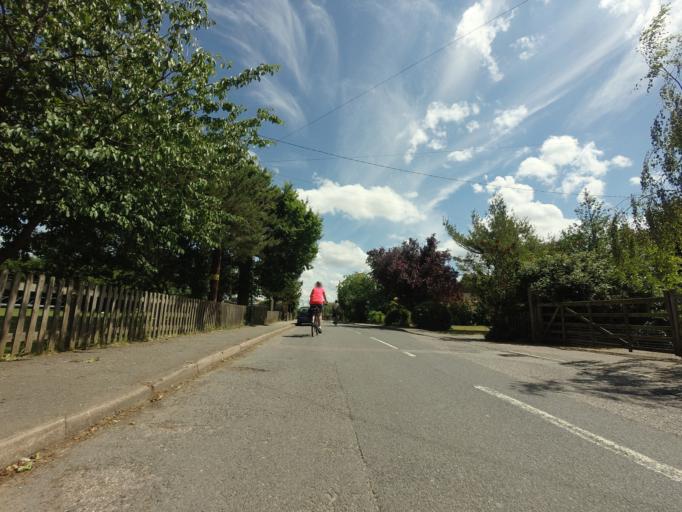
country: GB
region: England
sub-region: Medway
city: High Halstow
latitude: 51.4475
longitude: 0.5633
